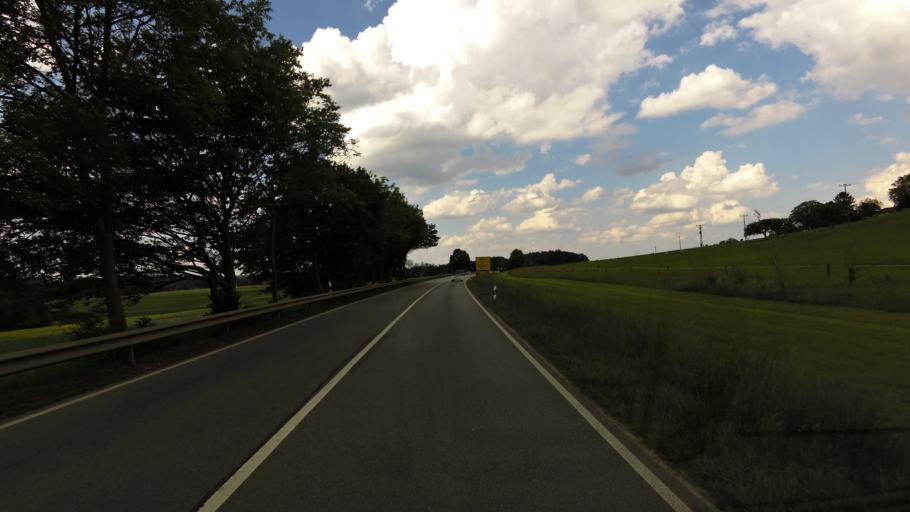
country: DE
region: Bavaria
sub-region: Upper Bavaria
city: Edling
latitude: 48.0374
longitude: 12.1788
